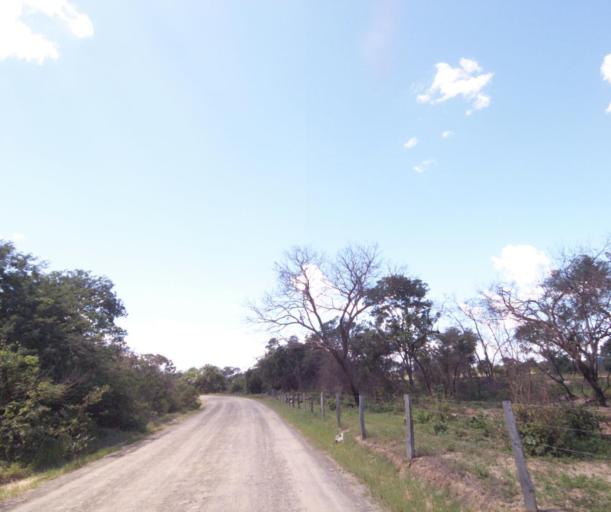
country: BR
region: Bahia
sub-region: Carinhanha
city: Carinhanha
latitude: -14.2297
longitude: -44.3054
